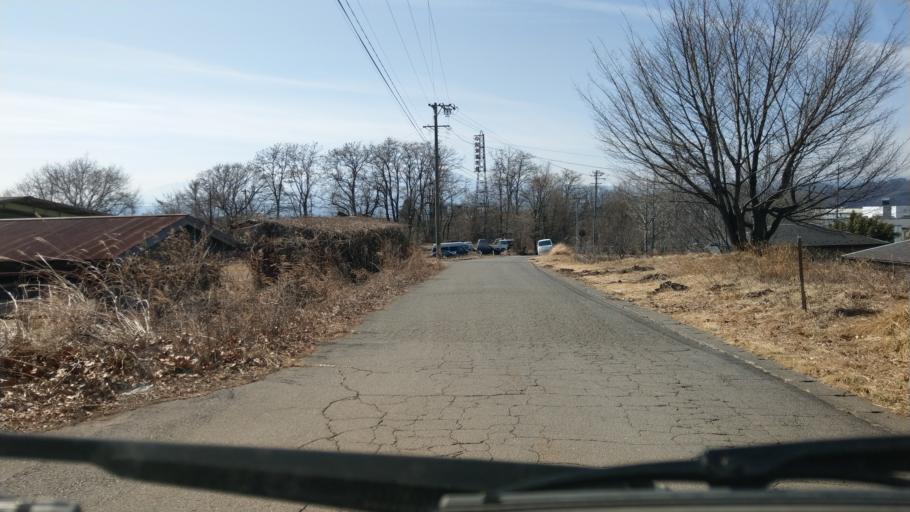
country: JP
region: Nagano
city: Komoro
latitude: 36.3169
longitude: 138.4465
